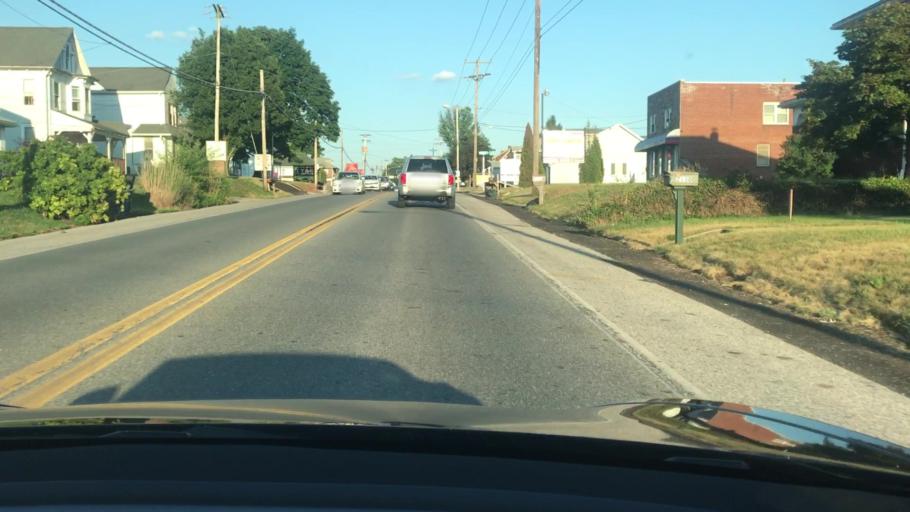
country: US
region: Pennsylvania
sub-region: York County
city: Shiloh
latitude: 39.9775
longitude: -76.7953
